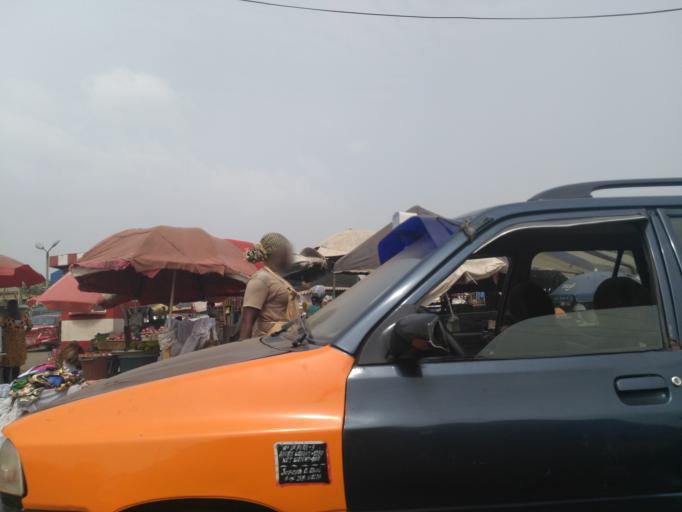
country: GH
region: Greater Accra
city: Accra
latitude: 5.5484
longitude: -0.2185
